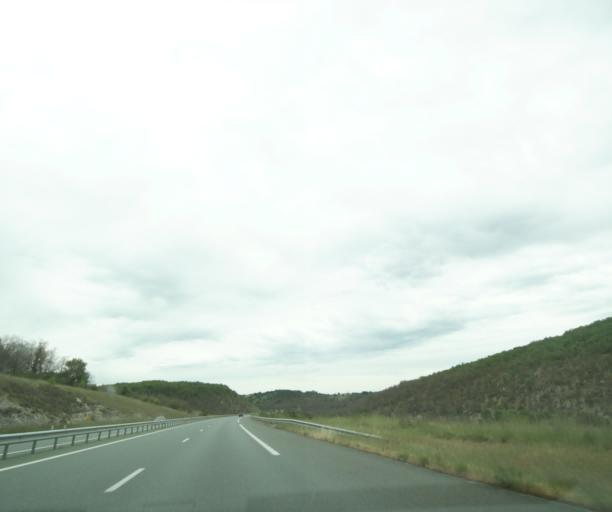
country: FR
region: Midi-Pyrenees
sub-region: Departement du Lot
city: Le Vigan
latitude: 44.7292
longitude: 1.5570
